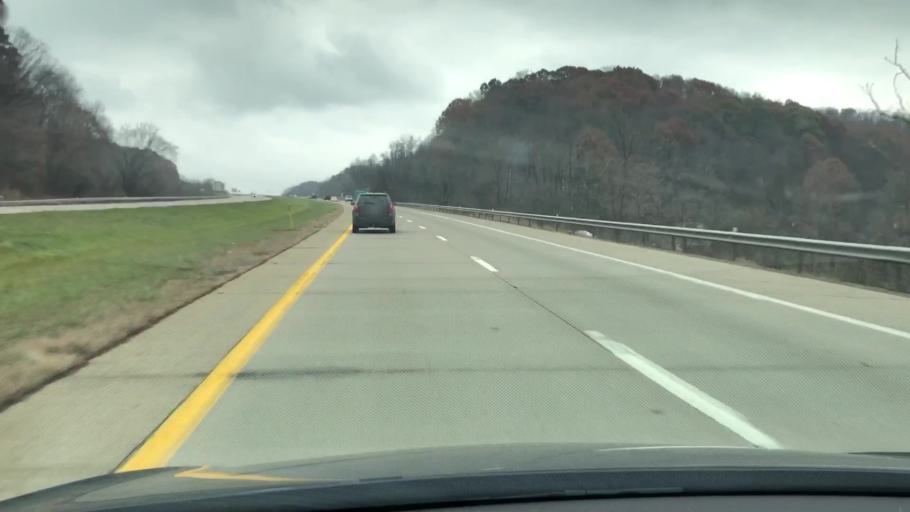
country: US
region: Pennsylvania
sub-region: Westmoreland County
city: New Stanton
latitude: 40.2079
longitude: -79.5875
